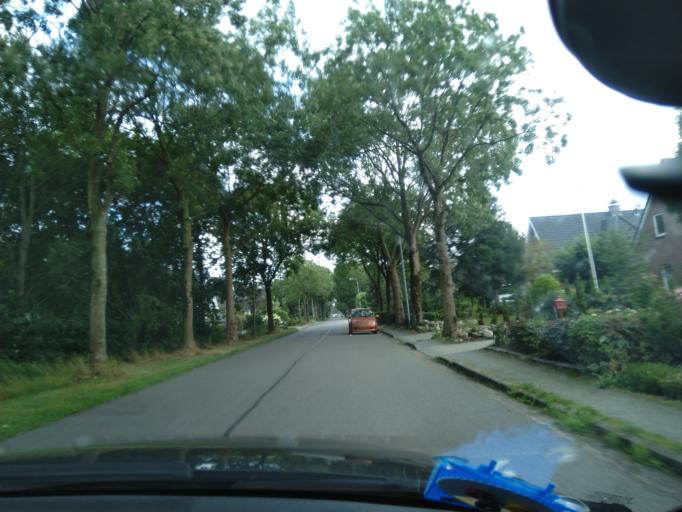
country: NL
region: Groningen
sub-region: Gemeente Zuidhorn
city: Aduard
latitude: 53.2261
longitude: 6.5001
